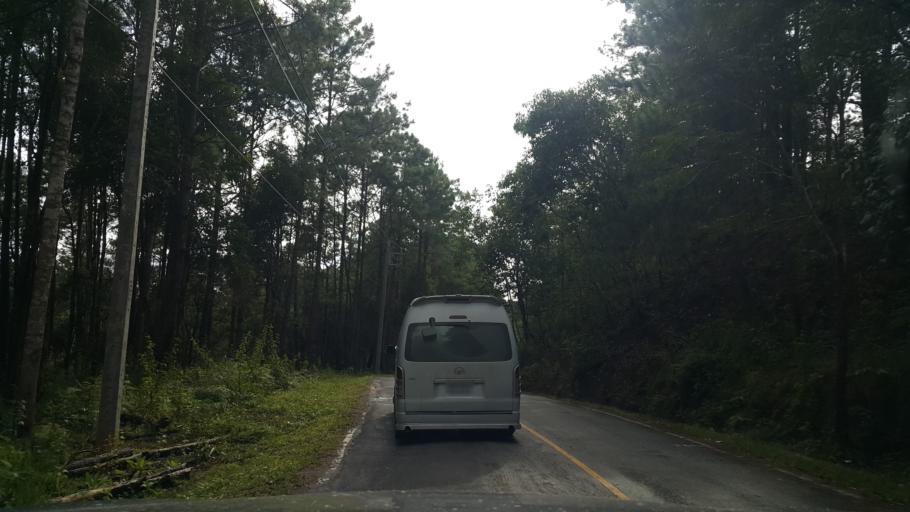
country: TH
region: Chiang Mai
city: Chaem Luang
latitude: 18.9329
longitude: 98.4744
